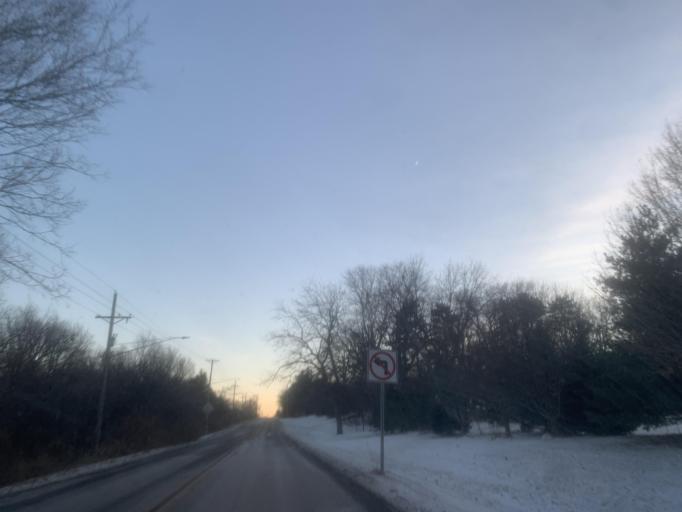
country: US
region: Nebraska
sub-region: Douglas County
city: Ralston
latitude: 41.2665
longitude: -96.0622
